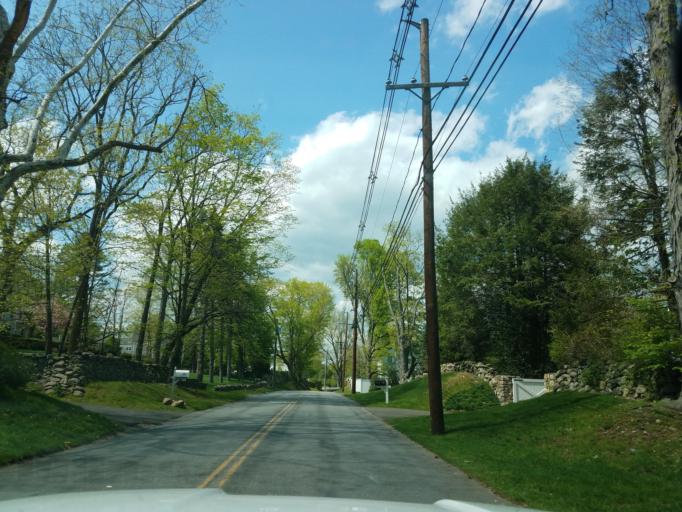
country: US
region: Connecticut
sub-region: Fairfield County
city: New Canaan
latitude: 41.1326
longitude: -73.4791
